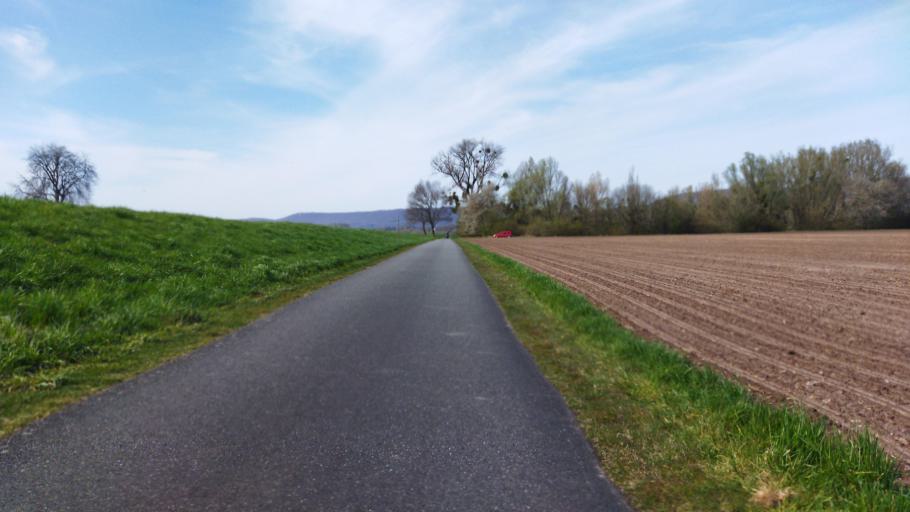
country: DE
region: Lower Saxony
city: Hessisch Oldendorf
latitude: 52.1534
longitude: 9.2730
